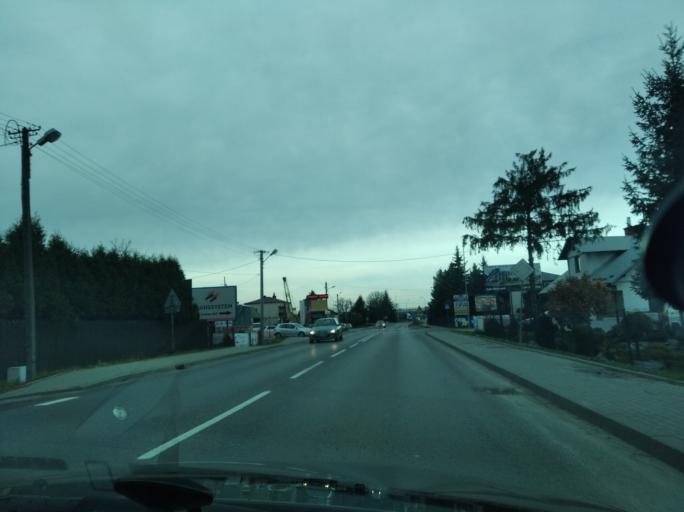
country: PL
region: Subcarpathian Voivodeship
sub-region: Powiat lancucki
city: Lancut
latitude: 50.0958
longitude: 22.2312
